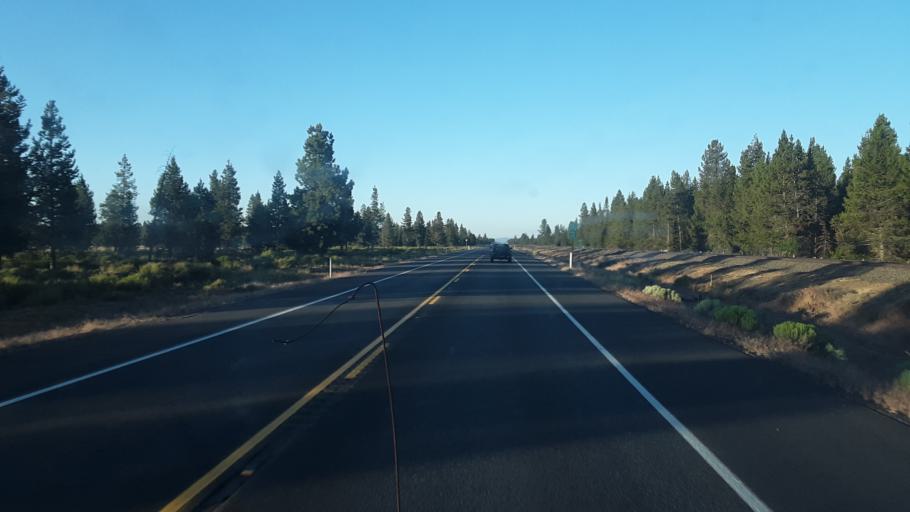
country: US
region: Oregon
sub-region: Deschutes County
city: La Pine
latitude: 43.7362
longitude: -121.4682
